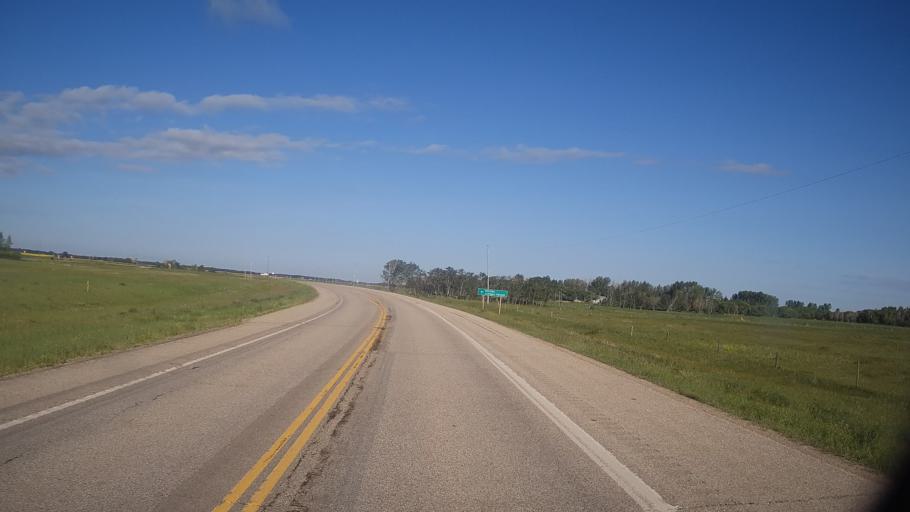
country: CA
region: Saskatchewan
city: Lanigan
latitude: 51.8752
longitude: -105.1861
